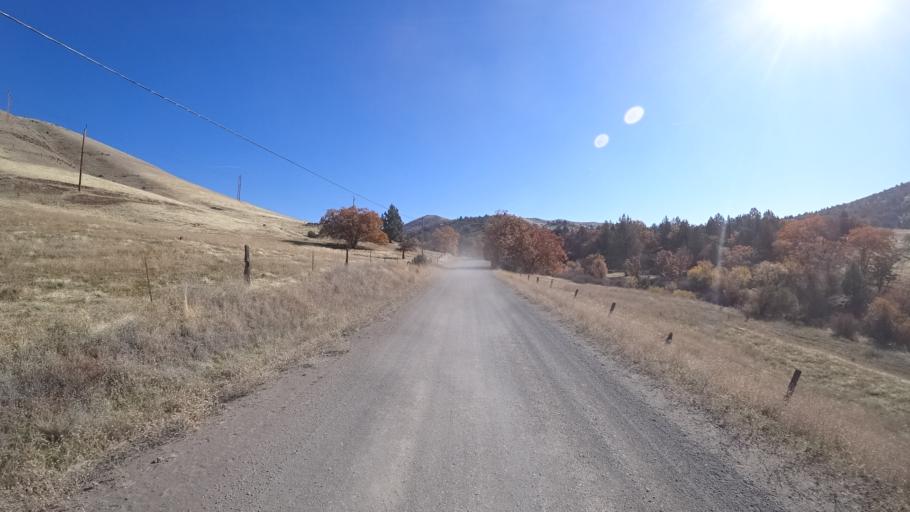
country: US
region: California
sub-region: Siskiyou County
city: Montague
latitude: 41.7949
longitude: -122.3640
